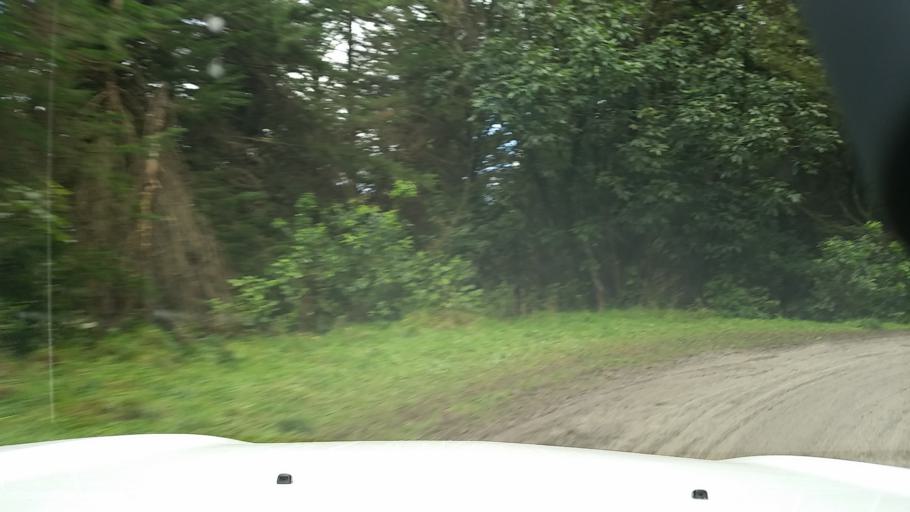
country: NZ
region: Wellington
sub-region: South Wairarapa District
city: Waipawa
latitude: -41.2595
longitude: 175.6184
